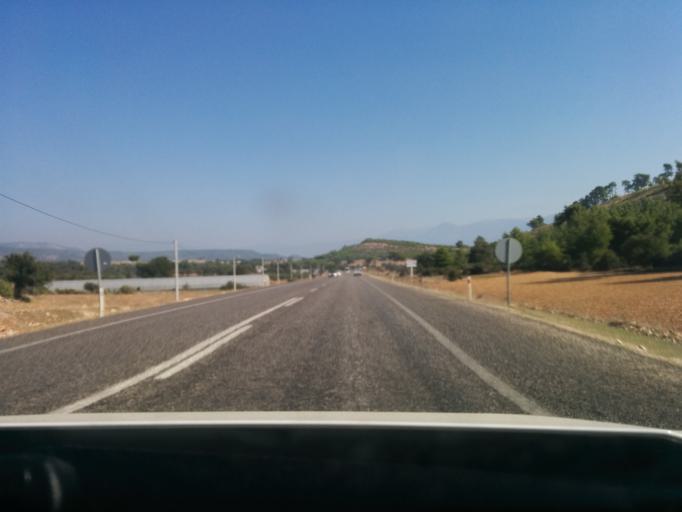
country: TR
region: Mugla
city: Esen
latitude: 36.4178
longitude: 29.2696
